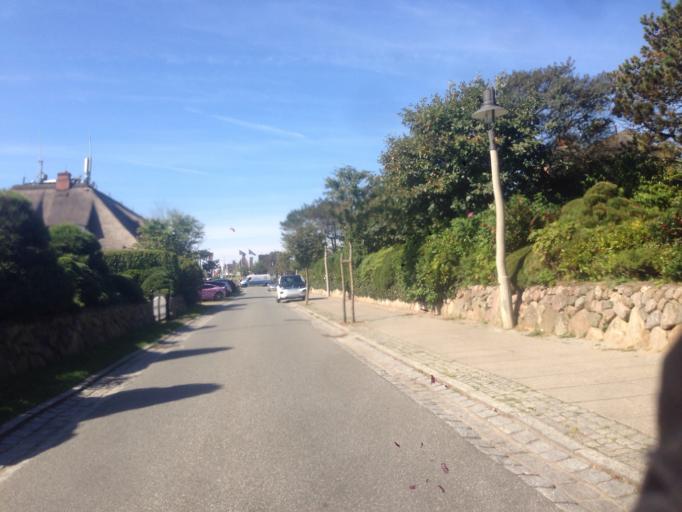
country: DE
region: Schleswig-Holstein
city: Tinnum
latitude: 54.9553
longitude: 8.3441
